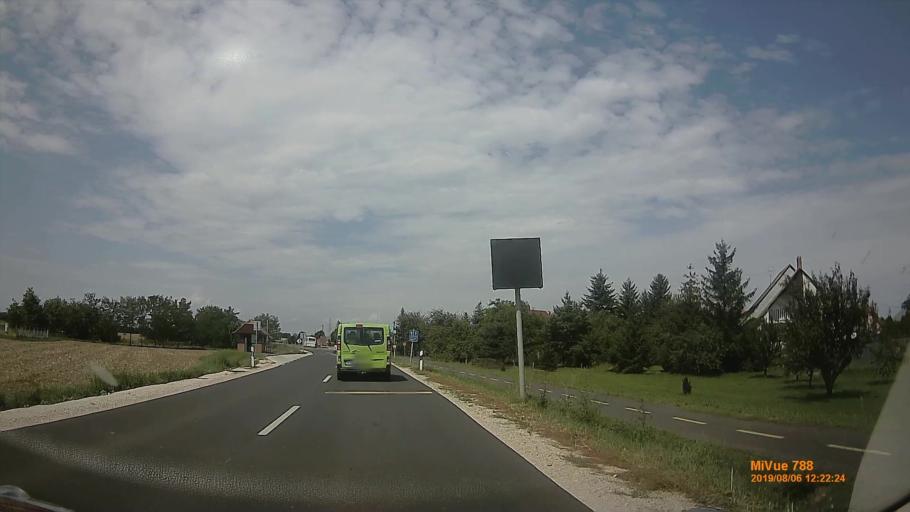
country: HU
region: Vas
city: Taplanszentkereszt
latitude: 47.1878
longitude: 16.7317
